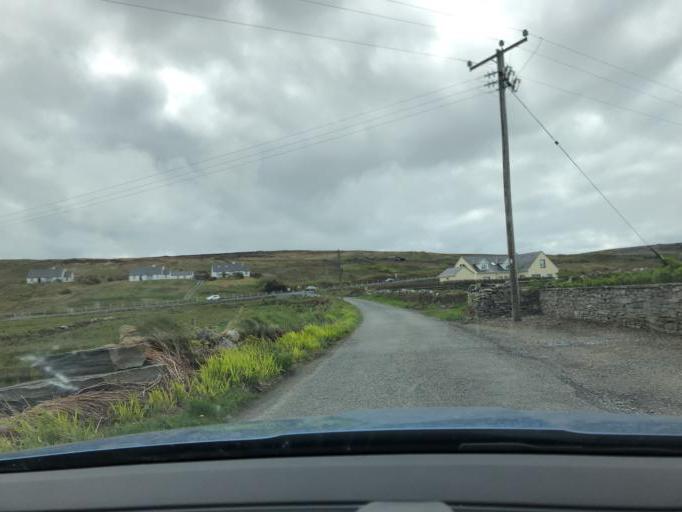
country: IE
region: Munster
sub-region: An Clar
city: Kilrush
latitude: 52.9917
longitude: -9.4058
